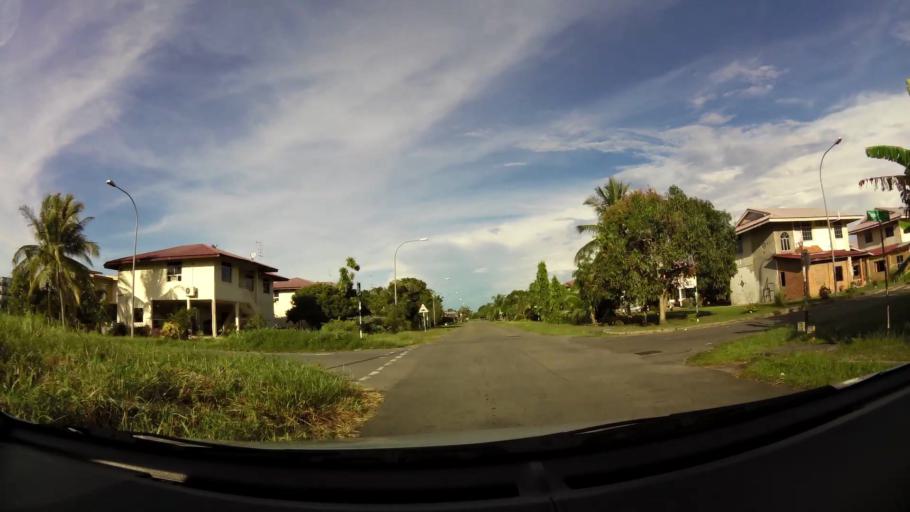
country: BN
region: Belait
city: Kuala Belait
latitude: 4.5784
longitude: 114.2234
